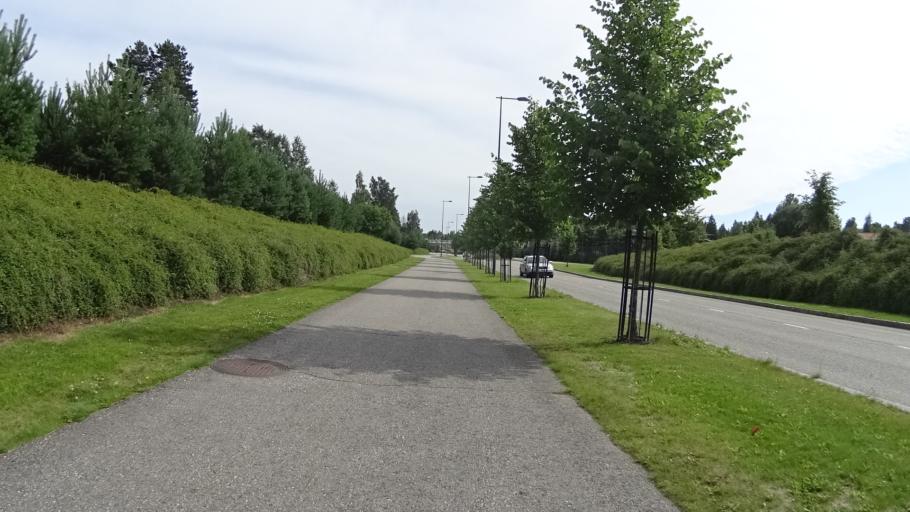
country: FI
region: Uusimaa
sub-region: Helsinki
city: Teekkarikylae
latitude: 60.2322
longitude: 24.8234
